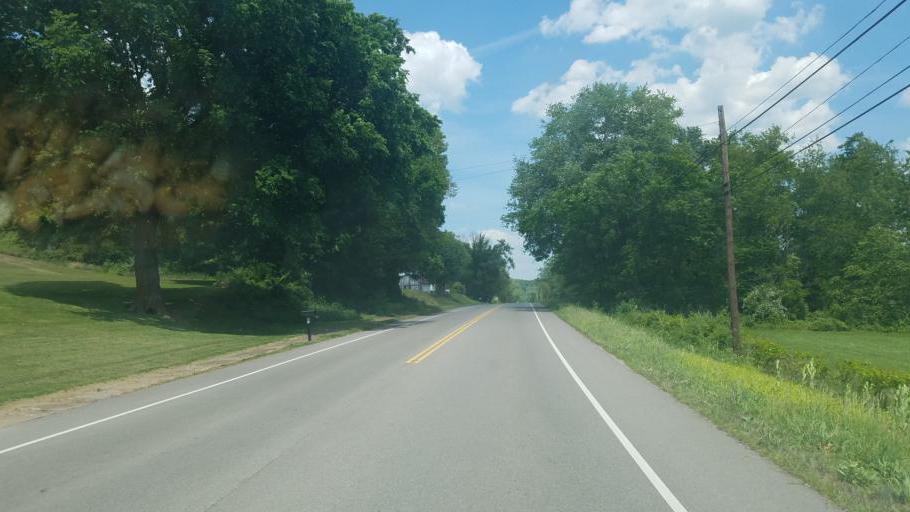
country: US
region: Ohio
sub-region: Meigs County
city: Middleport
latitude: 38.9841
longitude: -82.0853
